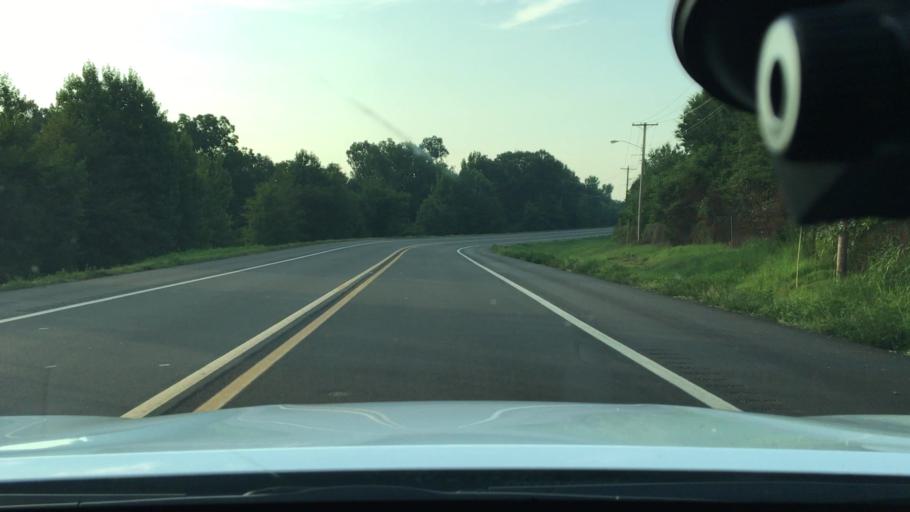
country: US
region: Arkansas
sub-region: Johnson County
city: Clarksville
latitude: 35.4527
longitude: -93.5309
